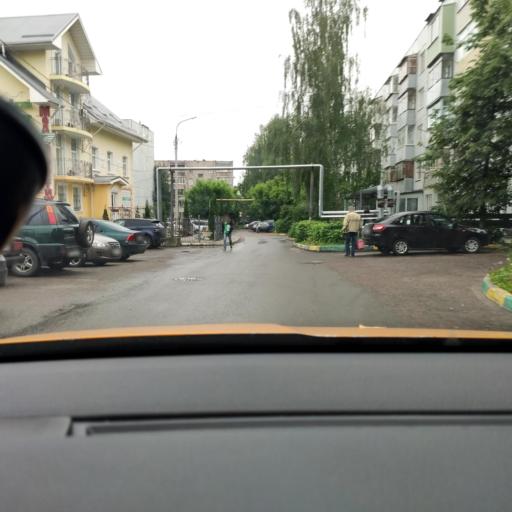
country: RU
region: Moskovskaya
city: Serpukhov
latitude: 54.9034
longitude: 37.4010
